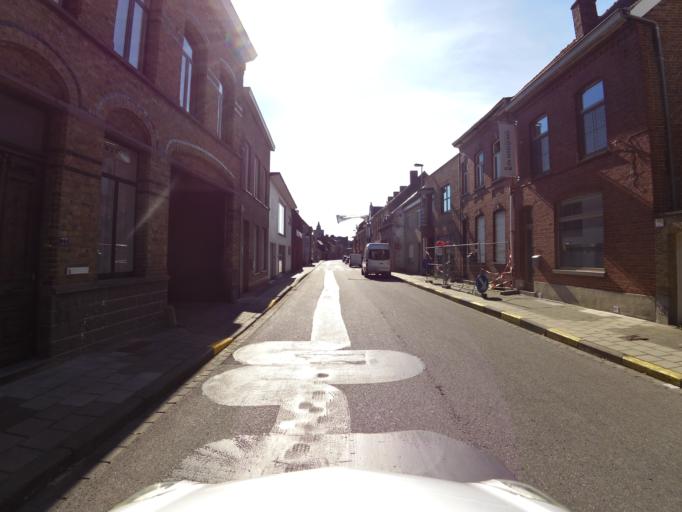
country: BE
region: Flanders
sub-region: Provincie West-Vlaanderen
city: Poperinge
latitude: 50.8589
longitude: 2.7292
